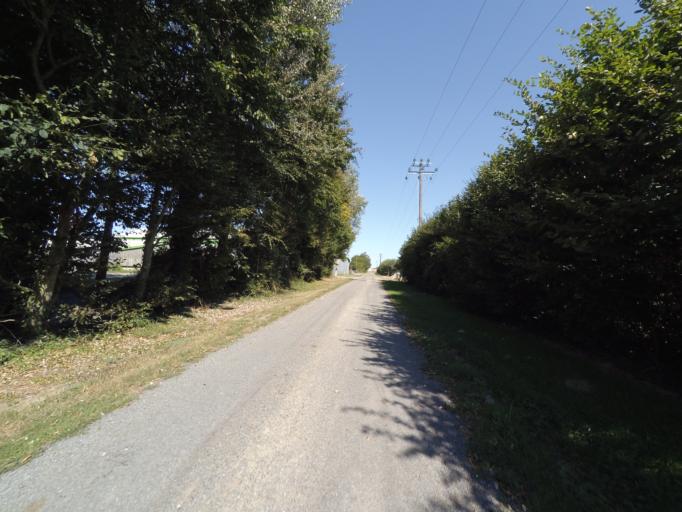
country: FR
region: Pays de la Loire
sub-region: Departement de la Loire-Atlantique
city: Vieillevigne
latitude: 46.9682
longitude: -1.4513
